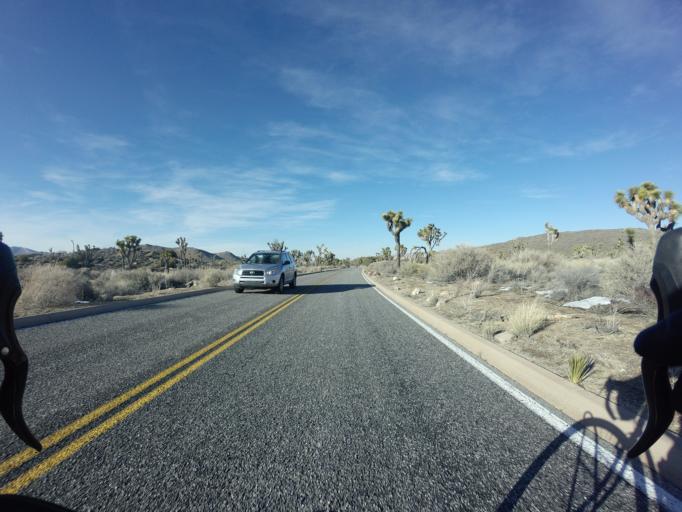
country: US
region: California
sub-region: Riverside County
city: Sky Valley
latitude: 33.9571
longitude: -116.1731
